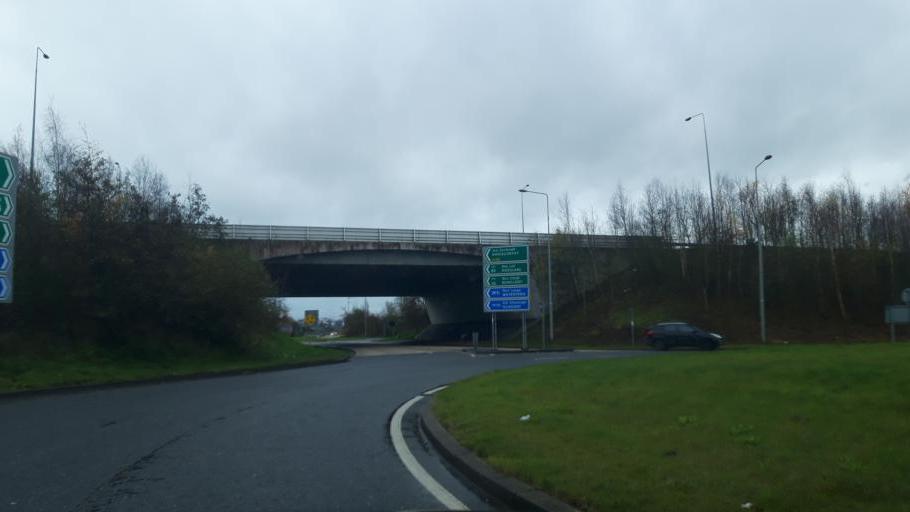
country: IE
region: Leinster
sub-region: County Carlow
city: Carlow
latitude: 52.8020
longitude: -6.8817
